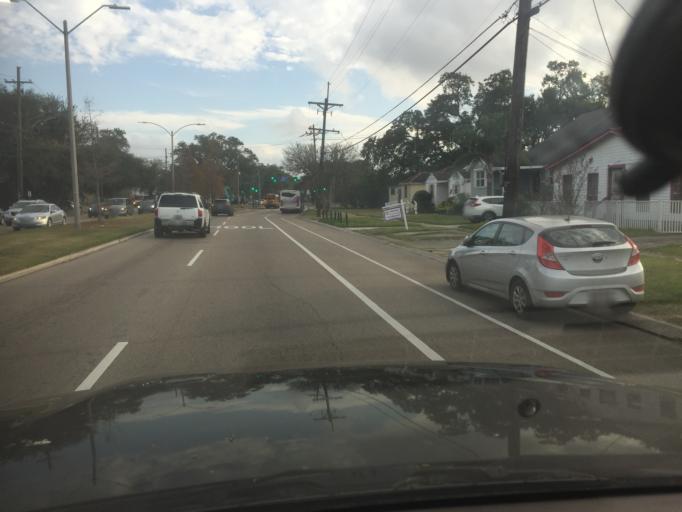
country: US
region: Louisiana
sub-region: Orleans Parish
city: New Orleans
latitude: 29.9896
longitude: -90.0754
